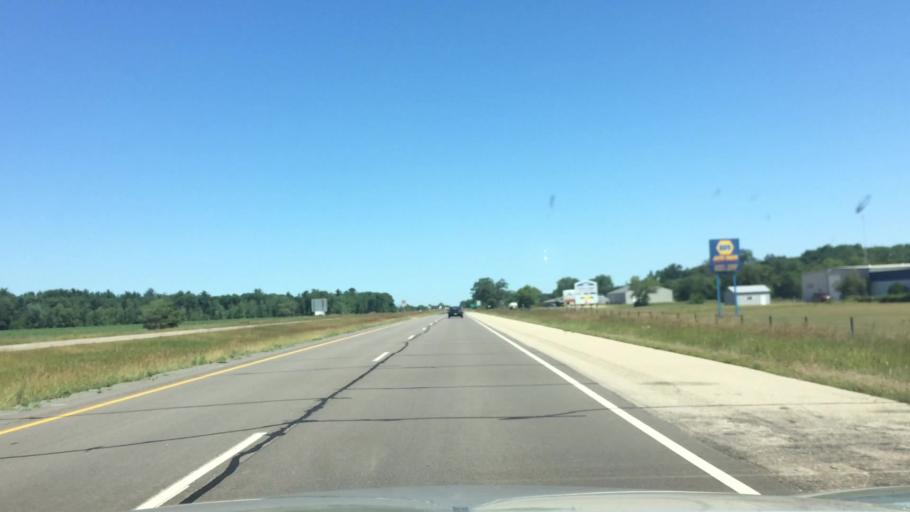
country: US
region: Wisconsin
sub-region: Portage County
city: Plover
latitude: 44.2210
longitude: -89.5243
